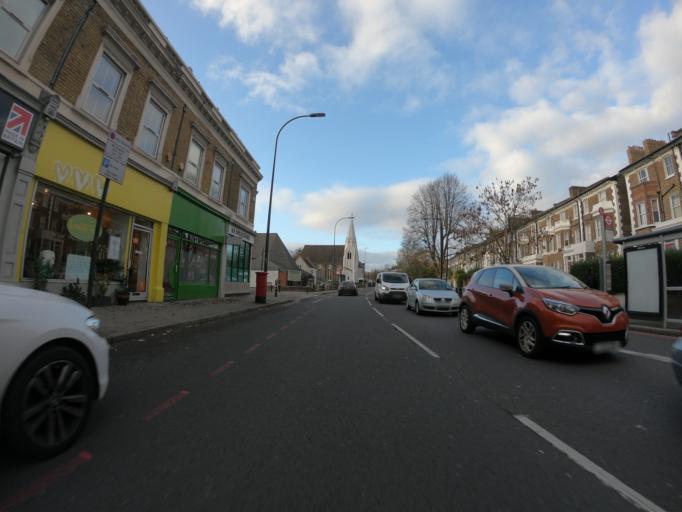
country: GB
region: England
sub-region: Greater London
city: Blackheath
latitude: 51.4570
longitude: 0.0092
